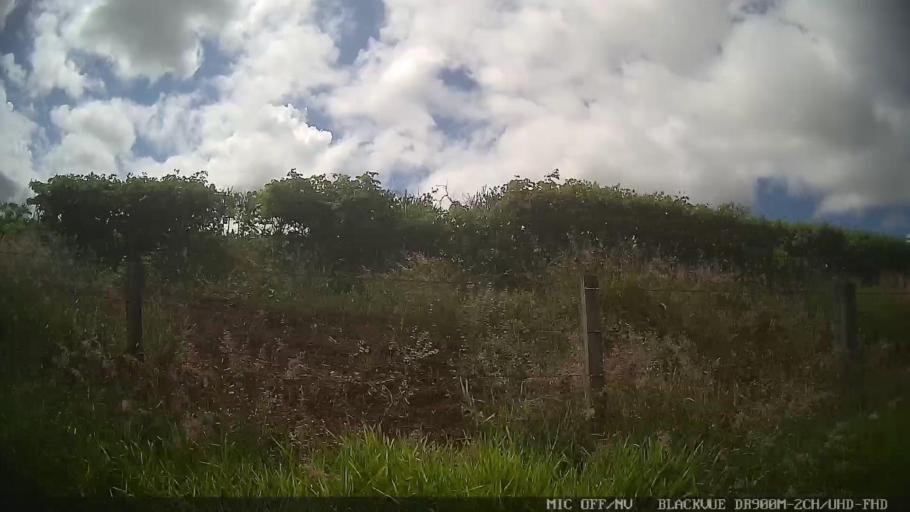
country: BR
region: Sao Paulo
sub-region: Amparo
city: Amparo
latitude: -22.8601
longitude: -46.7162
